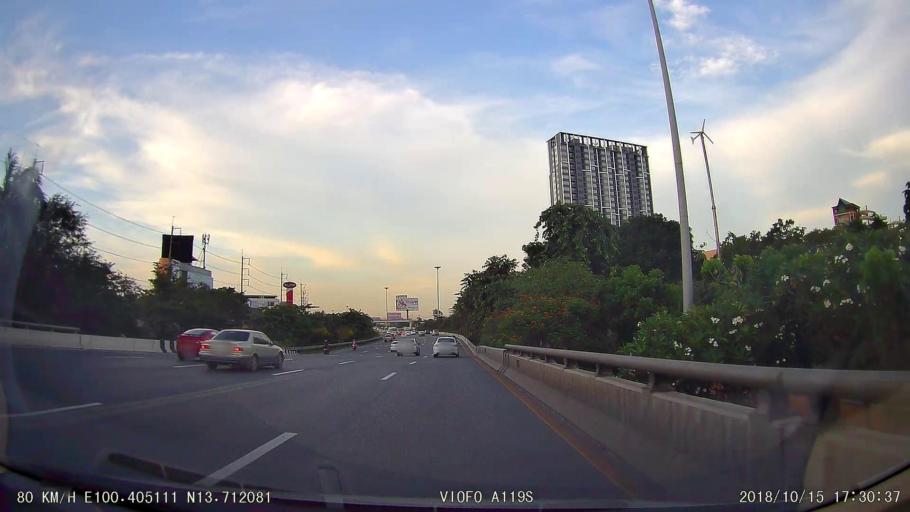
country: TH
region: Bangkok
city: Bang Khae
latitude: 13.7123
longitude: 100.4053
